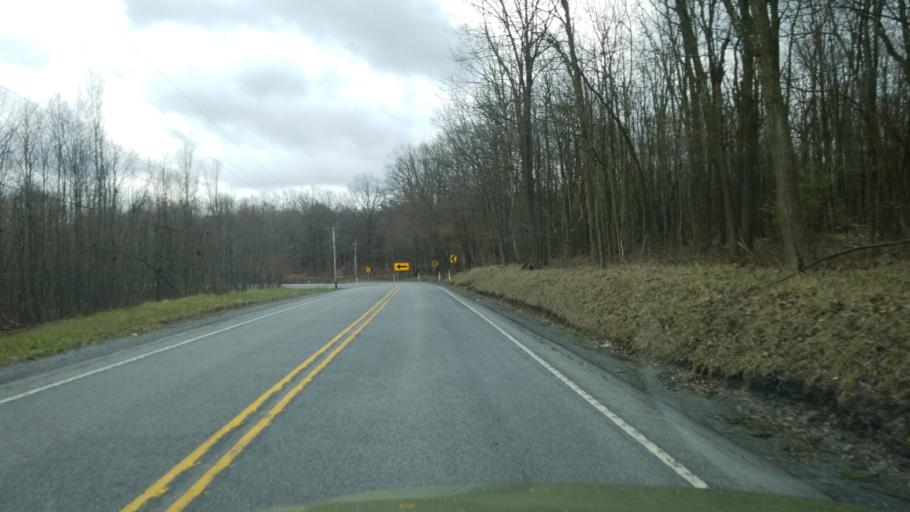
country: US
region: Pennsylvania
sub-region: Blair County
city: Tipton
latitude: 40.7299
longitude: -78.3707
